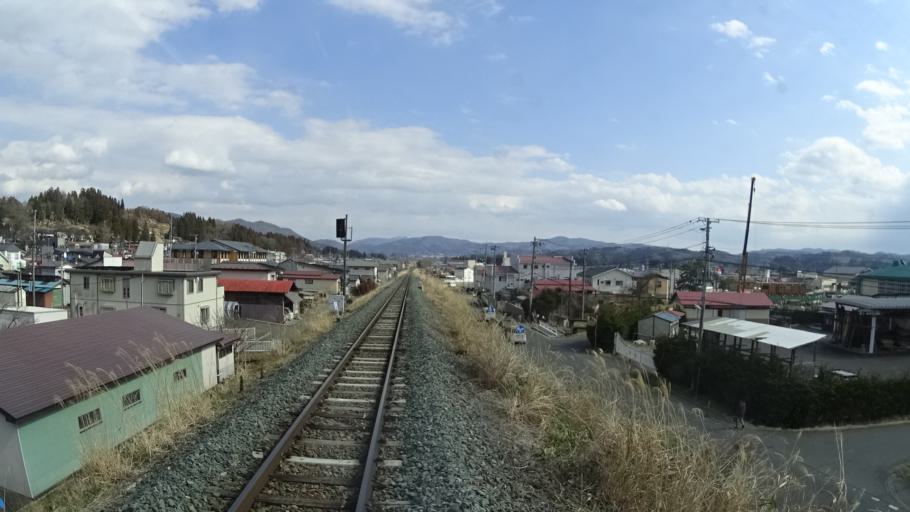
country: JP
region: Iwate
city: Hanamaki
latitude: 39.3873
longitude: 141.2263
